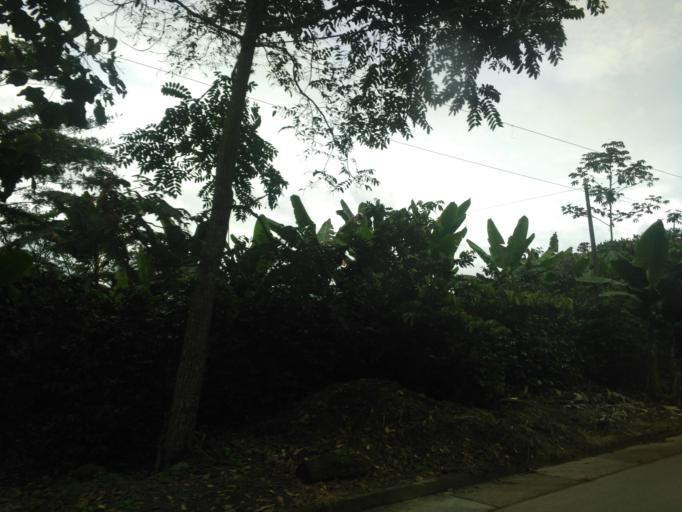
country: CO
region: Valle del Cauca
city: Sevilla
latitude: 4.2983
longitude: -75.9025
